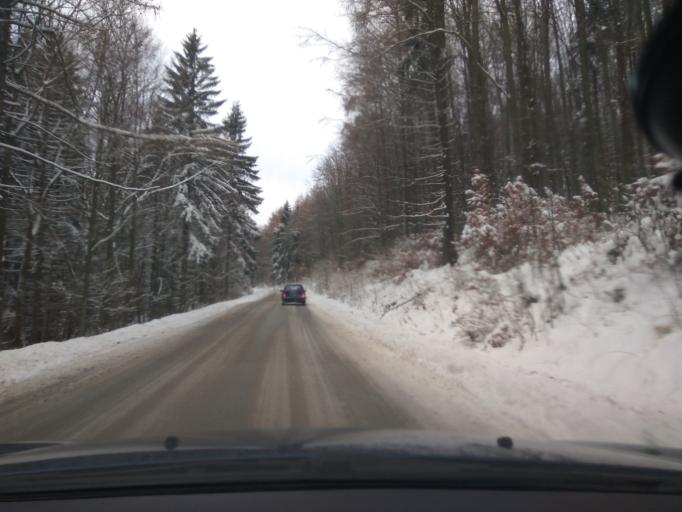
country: CZ
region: Zlin
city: Strani
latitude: 48.8498
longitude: 17.6864
